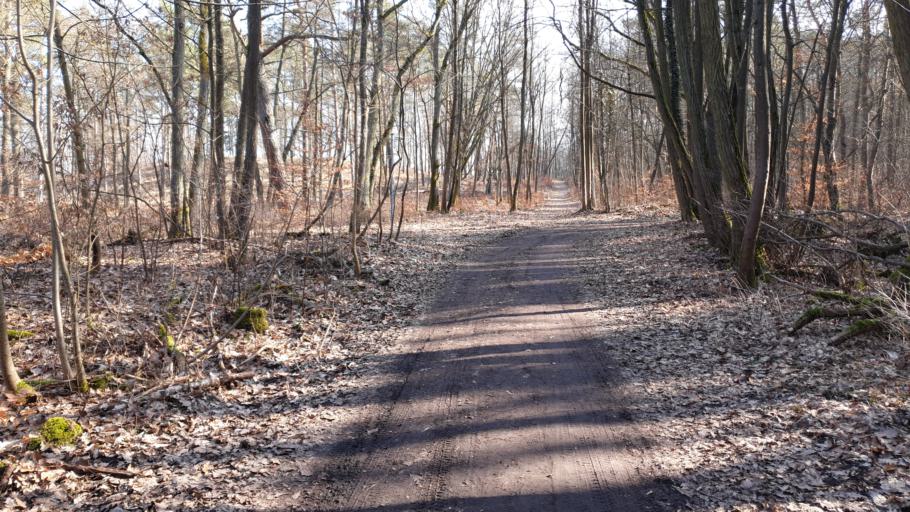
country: DE
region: Brandenburg
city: Strausberg
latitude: 52.5595
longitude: 13.8784
